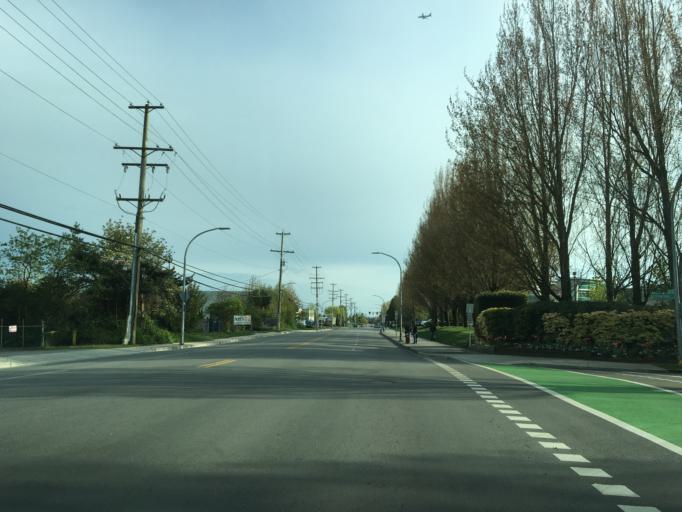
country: CA
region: British Columbia
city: Richmond
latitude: 49.1740
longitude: -123.0691
